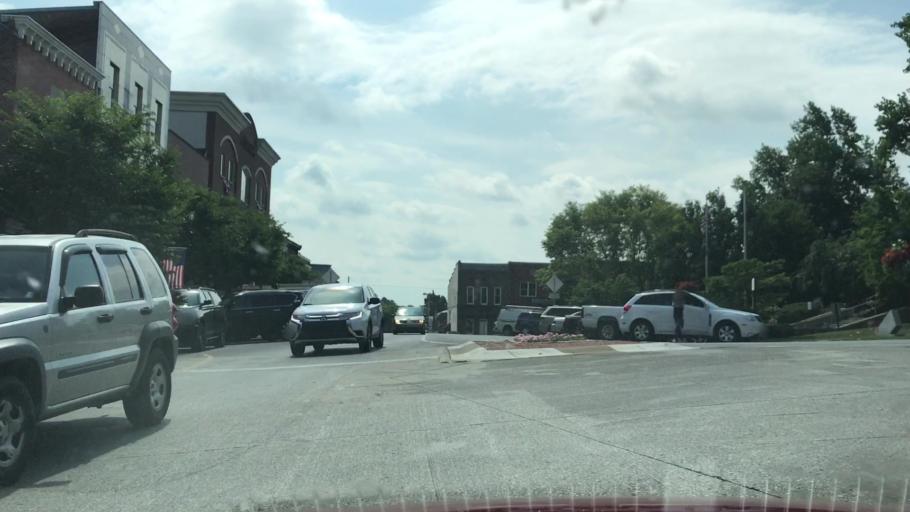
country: US
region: Kentucky
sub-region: Barren County
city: Glasgow
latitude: 36.9963
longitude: -85.9129
